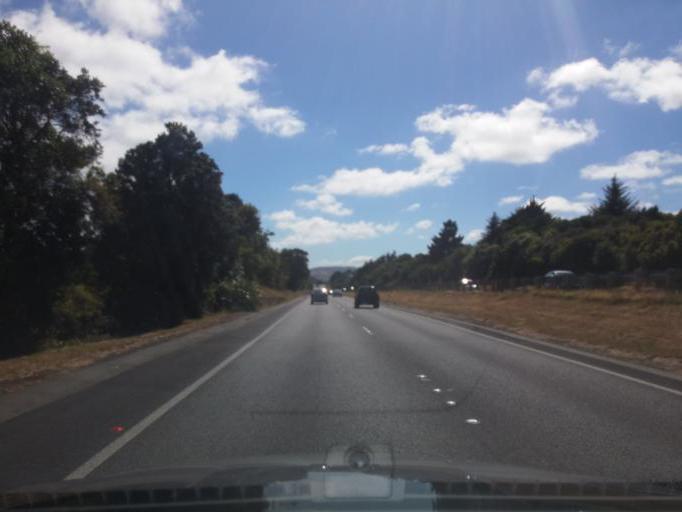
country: NZ
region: Wellington
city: Petone
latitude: -41.2161
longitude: 174.8122
